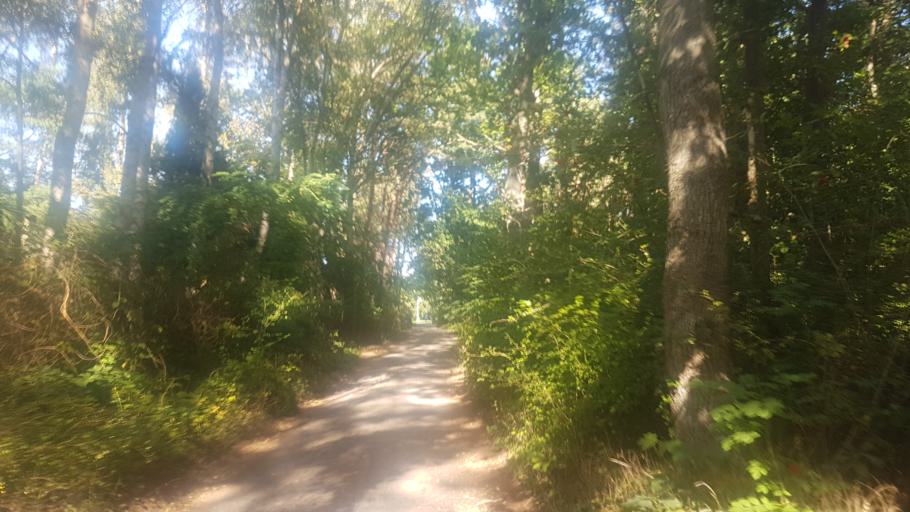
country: DE
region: Mecklenburg-Vorpommern
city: Altenkirchen
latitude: 54.6172
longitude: 13.3752
